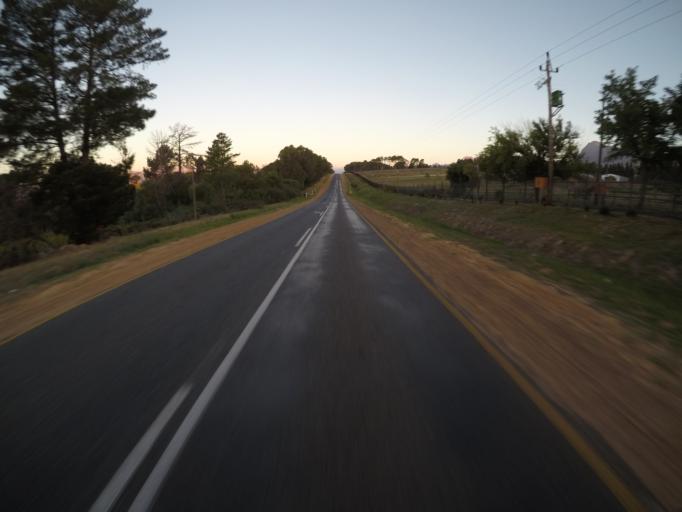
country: ZA
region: Western Cape
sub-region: Cape Winelands District Municipality
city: Paarl
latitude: -33.8106
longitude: 18.9072
